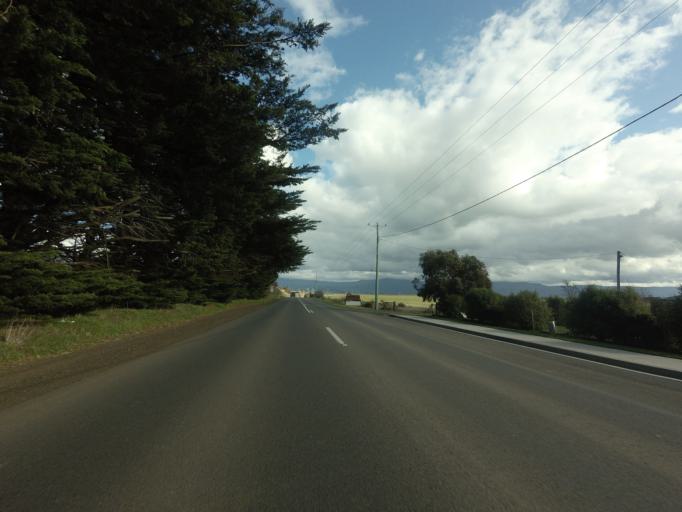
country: AU
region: Tasmania
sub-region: Northern Midlands
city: Longford
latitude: -41.6959
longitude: 147.0781
